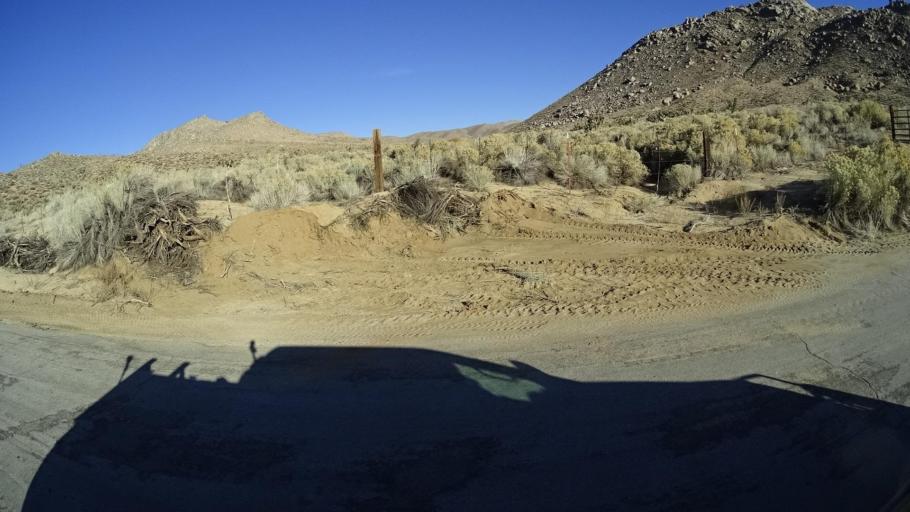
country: US
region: California
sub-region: Kern County
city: Weldon
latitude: 35.5055
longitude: -118.2021
